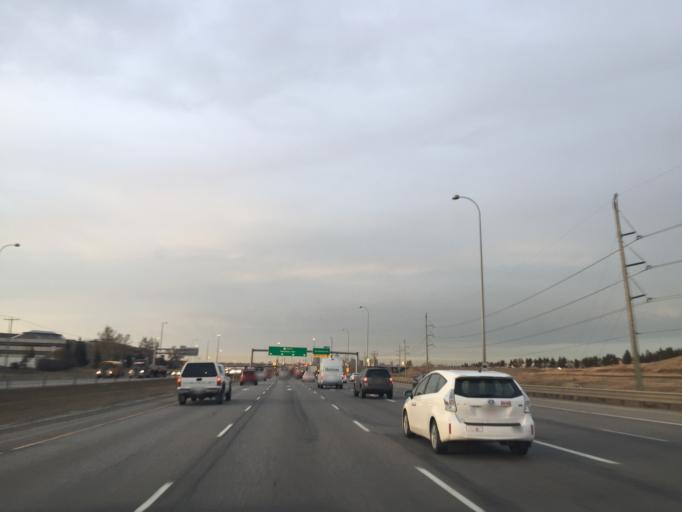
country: CA
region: Alberta
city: Calgary
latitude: 51.1173
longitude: -114.0469
